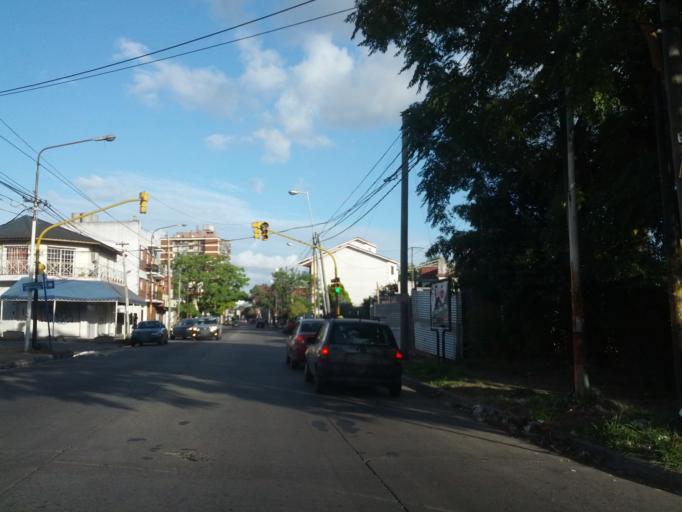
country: AR
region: Buenos Aires
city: Caseros
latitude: -34.6337
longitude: -58.5573
